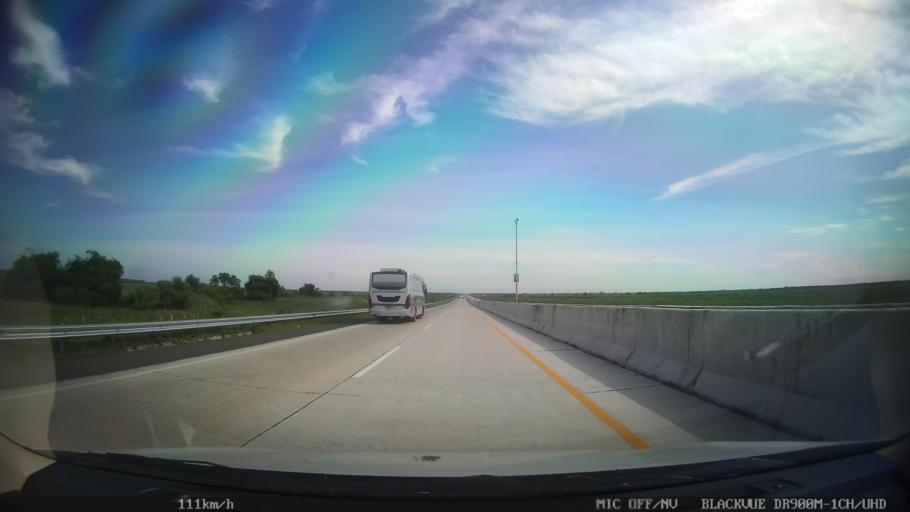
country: ID
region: North Sumatra
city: Binjai
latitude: 3.6683
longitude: 98.5337
